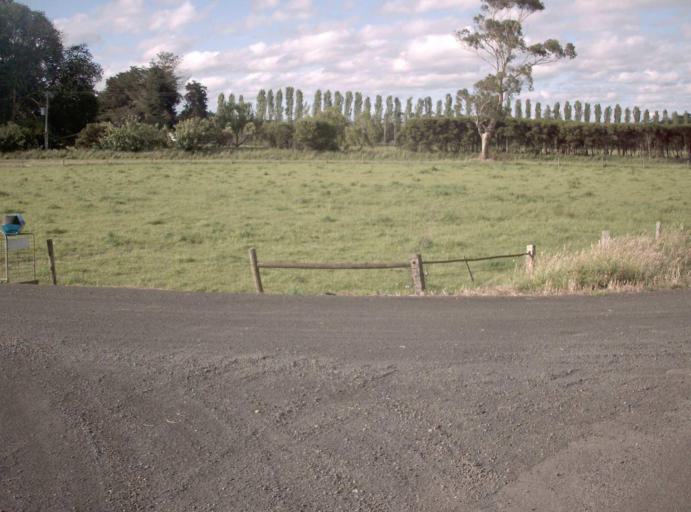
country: AU
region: Victoria
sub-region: Baw Baw
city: Warragul
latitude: -38.4922
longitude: 145.9289
